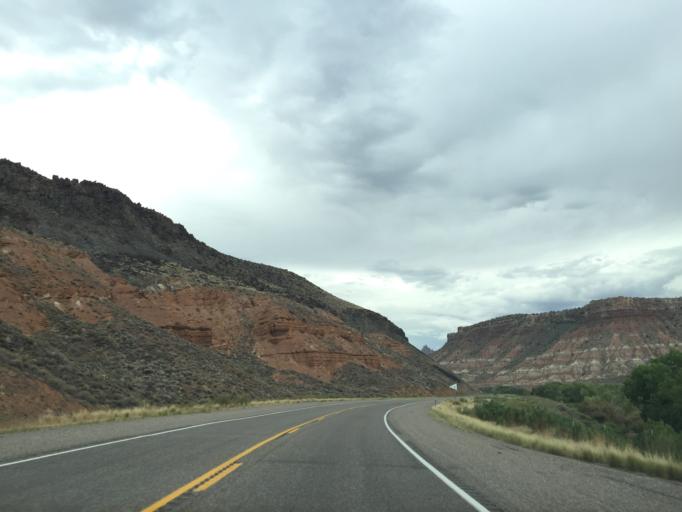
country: US
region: Utah
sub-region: Washington County
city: LaVerkin
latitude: 37.1724
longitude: -113.1104
